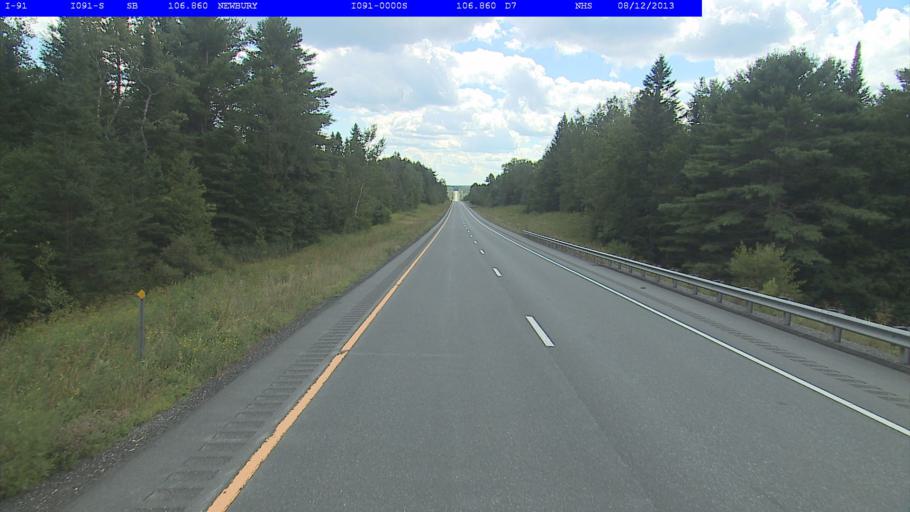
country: US
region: New Hampshire
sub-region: Grafton County
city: Woodsville
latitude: 44.1125
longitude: -72.1073
